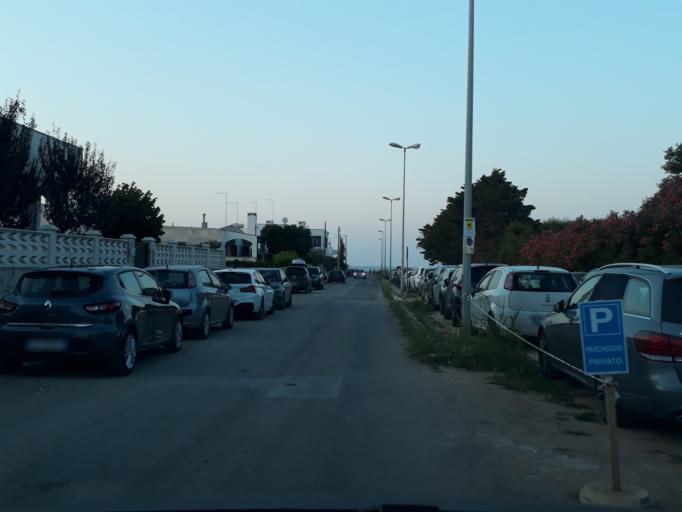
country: IT
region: Apulia
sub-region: Provincia di Brindisi
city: Carovigno
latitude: 40.7539
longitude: 17.7102
